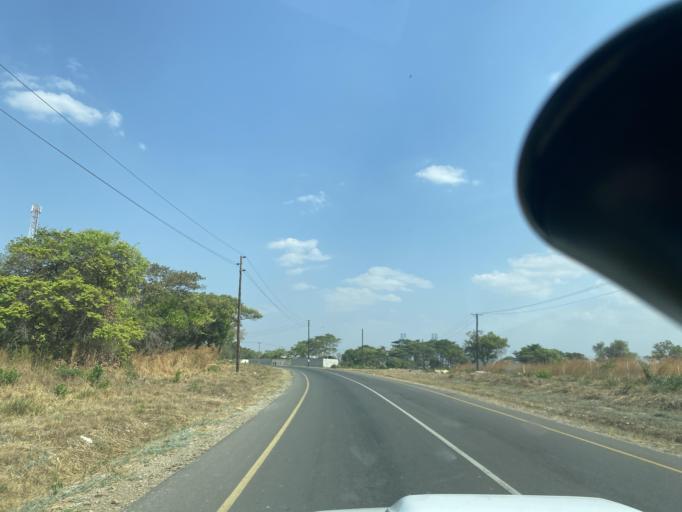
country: ZM
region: Lusaka
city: Lusaka
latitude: -15.3396
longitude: 28.0762
